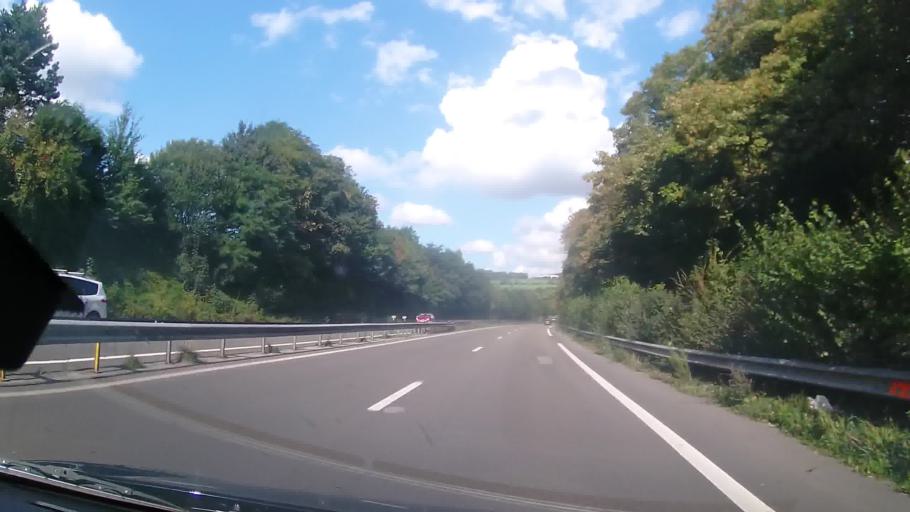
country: FR
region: Nord-Pas-de-Calais
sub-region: Departement du Pas-de-Calais
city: Wimille
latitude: 50.7591
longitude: 1.6331
